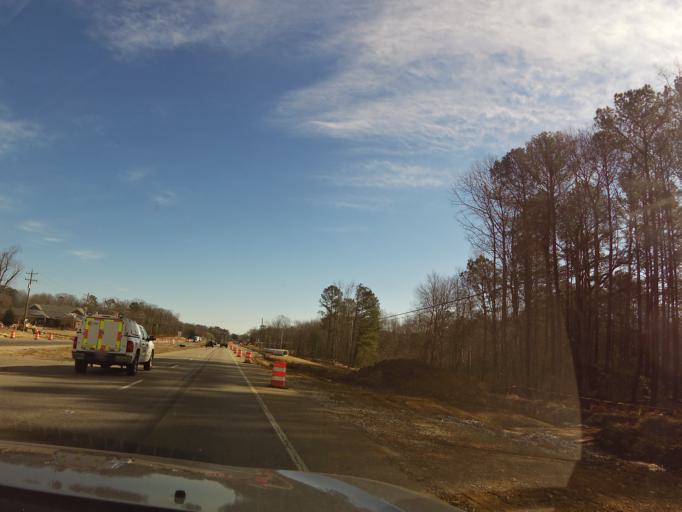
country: US
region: Virginia
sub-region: Chesterfield County
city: Enon
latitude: 37.3495
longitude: -77.3688
